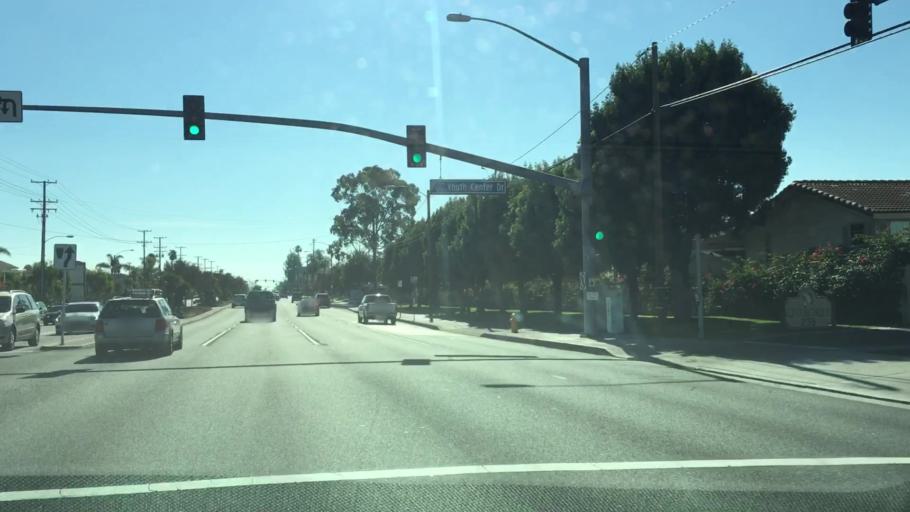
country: US
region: California
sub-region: Orange County
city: Stanton
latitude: 33.8284
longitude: -117.9935
